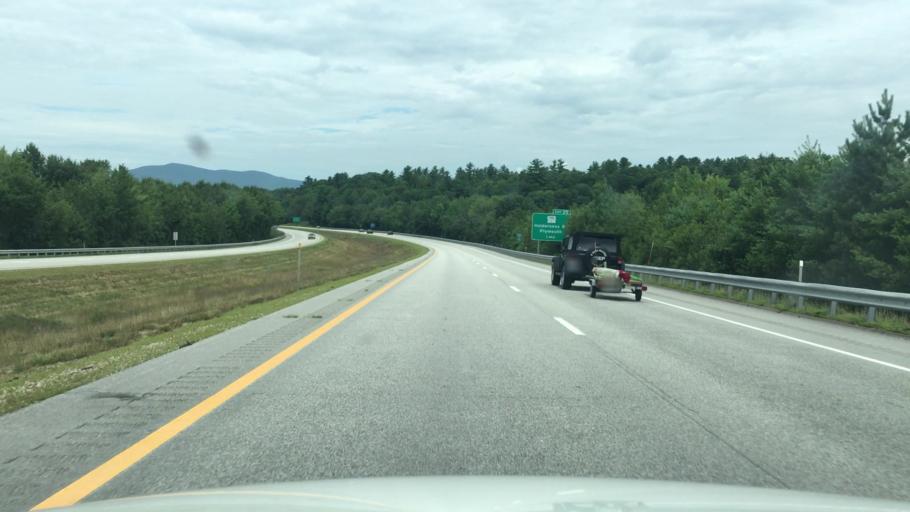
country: US
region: New Hampshire
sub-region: Grafton County
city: Plymouth
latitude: 43.7481
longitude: -71.6651
